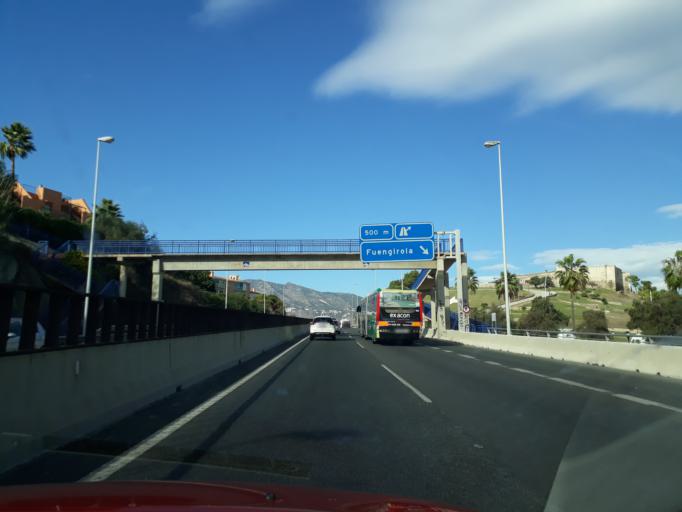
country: ES
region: Andalusia
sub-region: Provincia de Malaga
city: Fuengirola
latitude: 36.5230
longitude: -4.6301
